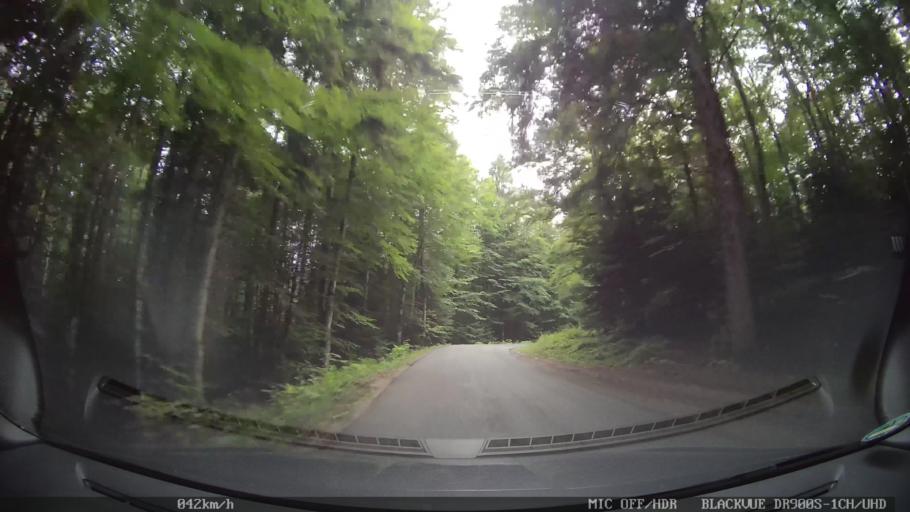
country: HR
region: Licko-Senjska
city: Jezerce
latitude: 44.9275
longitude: 15.5798
